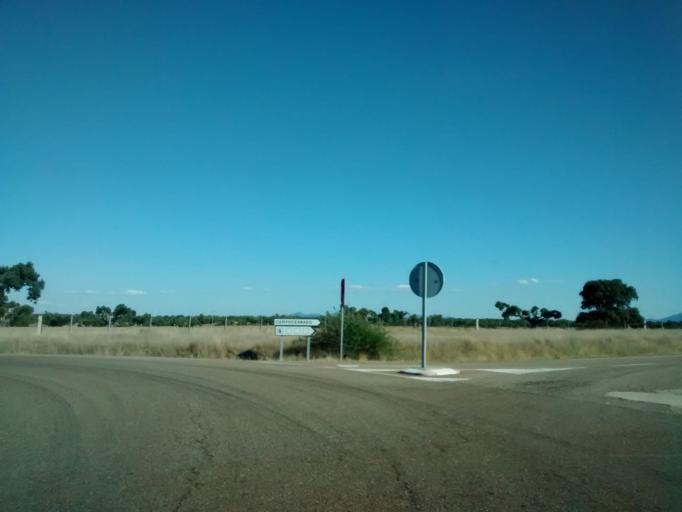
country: ES
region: Castille and Leon
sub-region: Provincia de Salamanca
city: Martin de Yeltes
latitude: 40.7707
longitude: -6.2861
